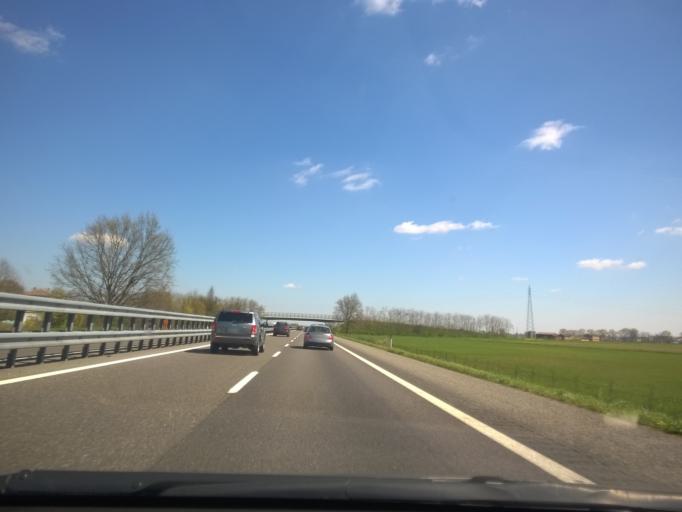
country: IT
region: Emilia-Romagna
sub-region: Provincia di Piacenza
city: Sarmato
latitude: 45.0722
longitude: 9.4786
